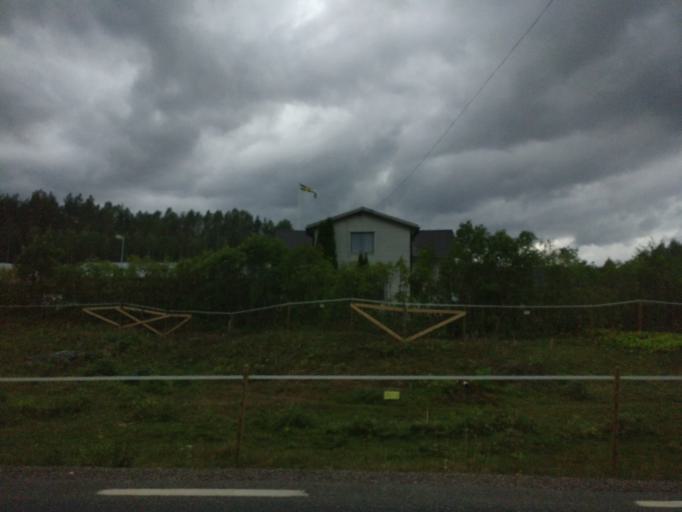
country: SE
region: Vaermland
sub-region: Torsby Kommun
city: Torsby
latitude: 60.6182
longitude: 13.0390
